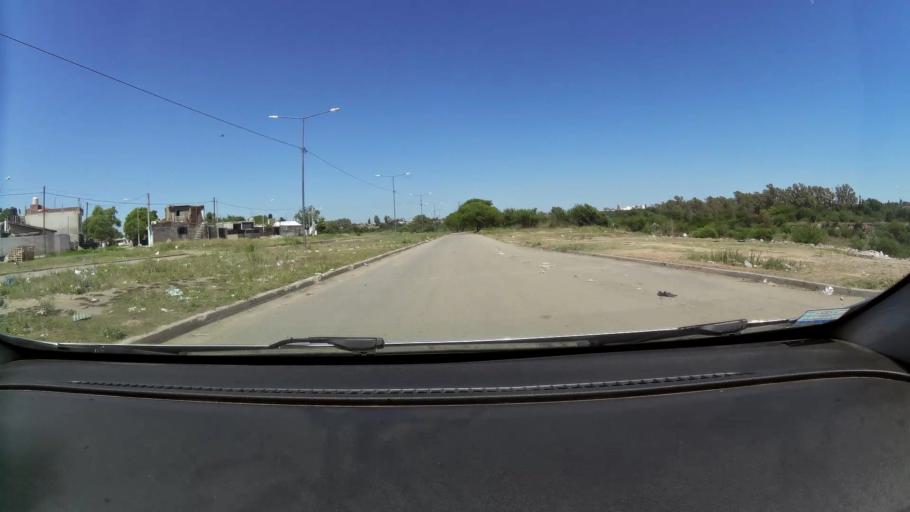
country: AR
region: Cordoba
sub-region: Departamento de Capital
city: Cordoba
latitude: -31.4072
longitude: -64.1391
